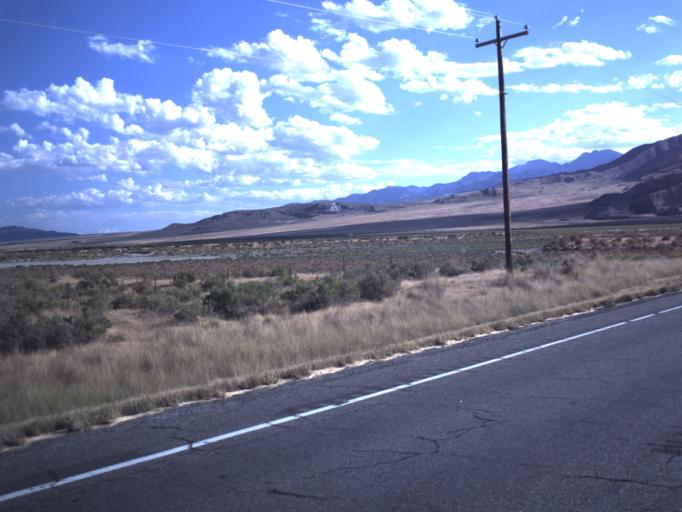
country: US
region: Utah
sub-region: Tooele County
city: Grantsville
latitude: 40.6893
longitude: -112.5387
